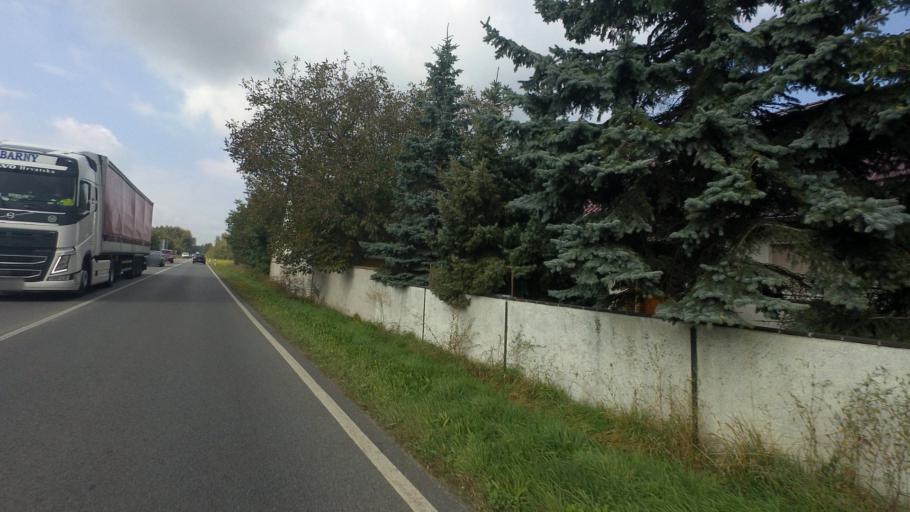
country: DE
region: Brandenburg
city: Hohenleipisch
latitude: 51.4704
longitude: 13.5660
